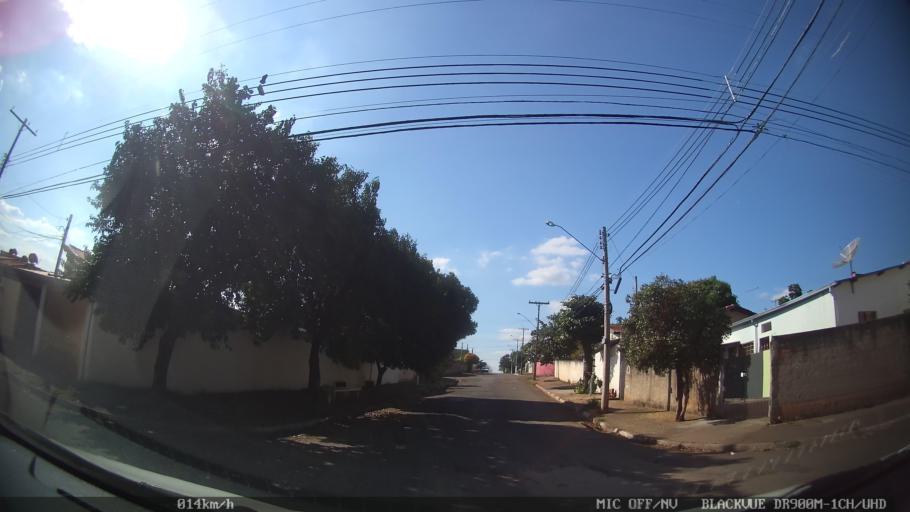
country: BR
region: Sao Paulo
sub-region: Sumare
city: Sumare
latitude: -22.8169
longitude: -47.2930
